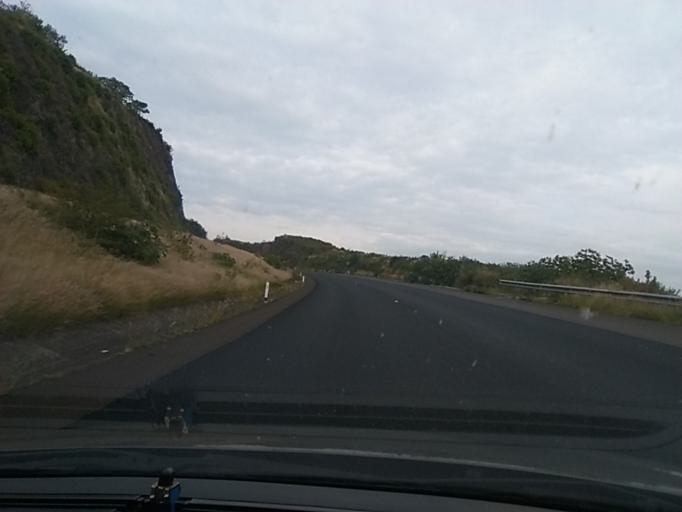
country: MX
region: Mexico
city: Huaniqueo de Morales
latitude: 19.8897
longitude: -101.5614
